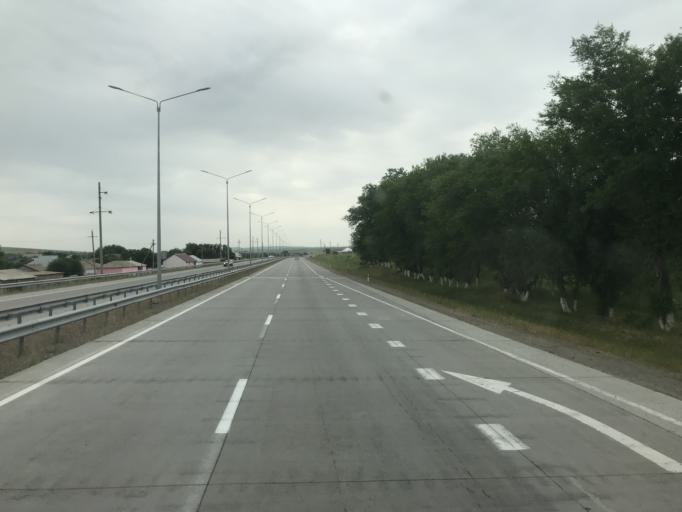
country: KZ
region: Ongtustik Qazaqstan
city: Qazyqurt
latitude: 41.8830
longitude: 69.4391
